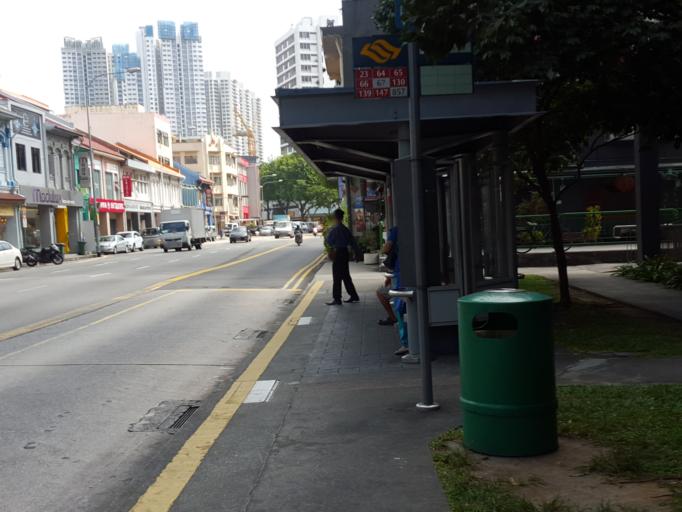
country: SG
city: Singapore
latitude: 1.3104
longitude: 103.8584
